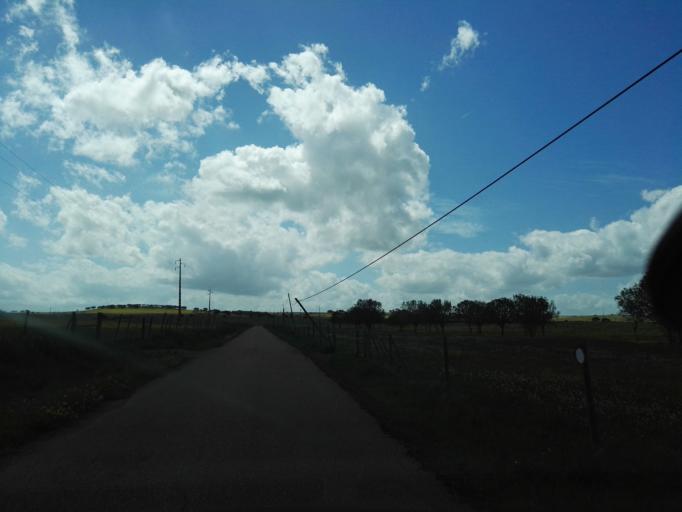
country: PT
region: Portalegre
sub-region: Elvas
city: Elvas
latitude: 38.9671
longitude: -7.1727
